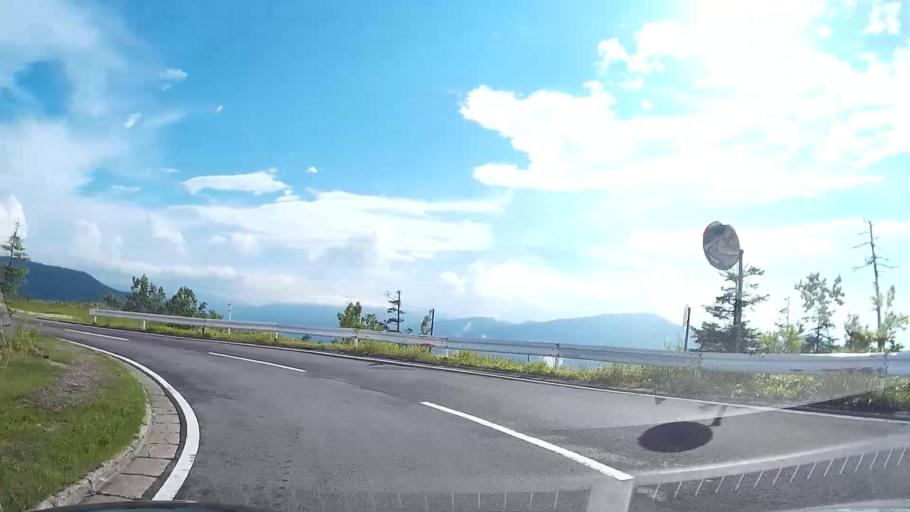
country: JP
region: Nagano
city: Nakano
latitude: 36.6423
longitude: 138.5198
